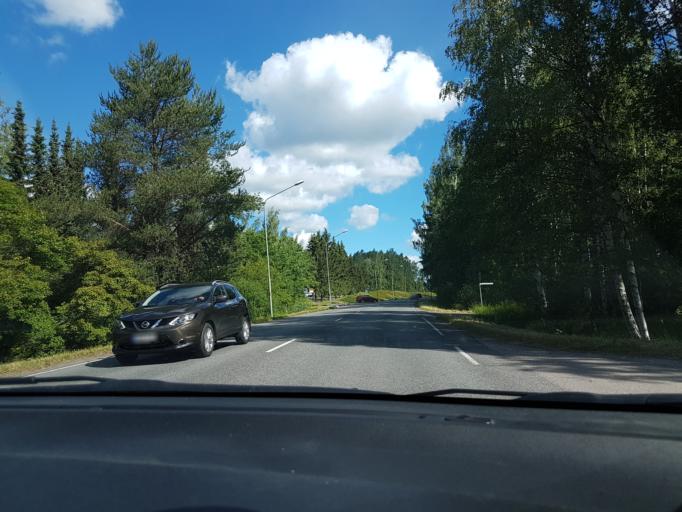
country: FI
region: Uusimaa
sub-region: Helsinki
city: Kerava
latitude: 60.3856
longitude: 25.0983
